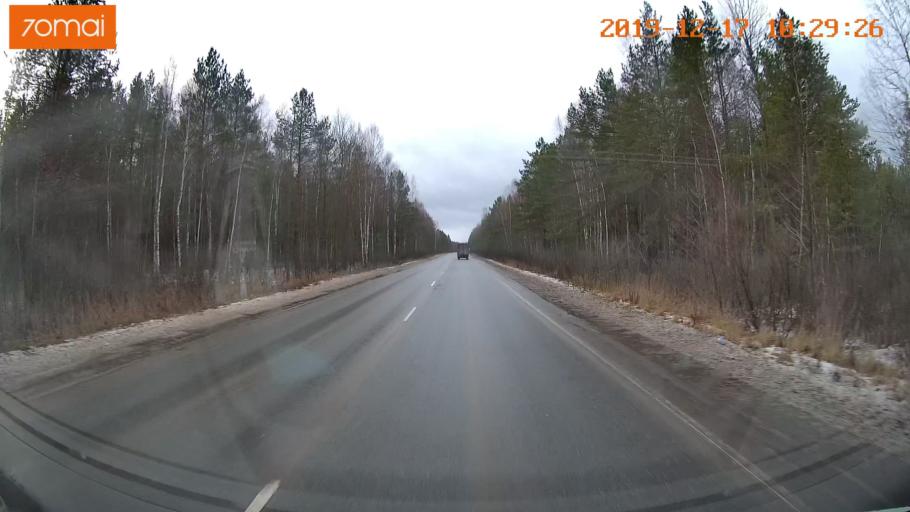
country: RU
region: Vladimir
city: Anopino
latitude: 55.6522
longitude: 40.7206
